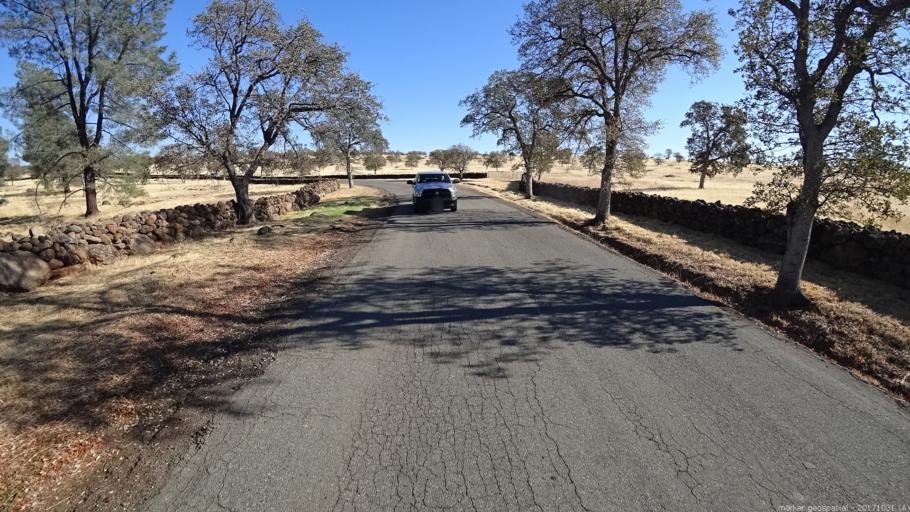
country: US
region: California
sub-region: Shasta County
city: Shingletown
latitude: 40.4605
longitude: -122.0731
